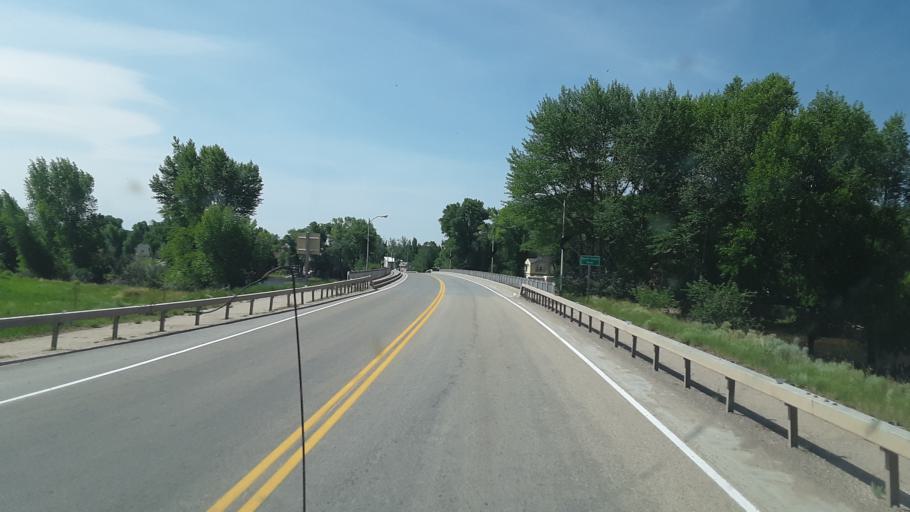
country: US
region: Wyoming
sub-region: Carbon County
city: Saratoga
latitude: 41.4600
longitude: -106.8073
